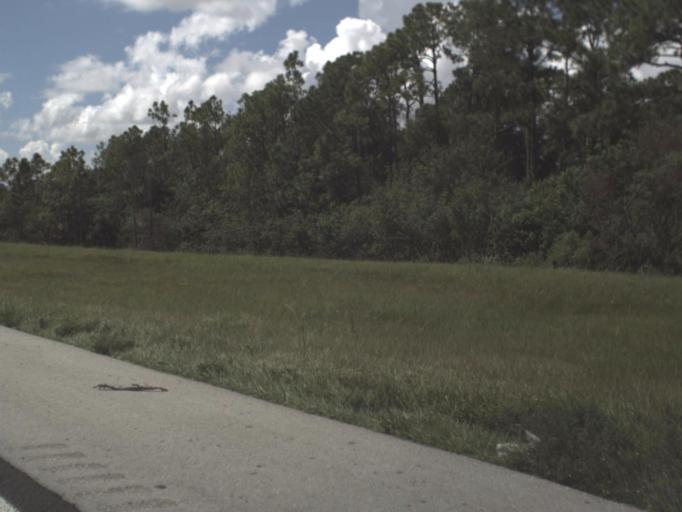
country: US
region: Florida
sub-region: Lee County
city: Fort Myers
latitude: 26.5963
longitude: -81.7986
